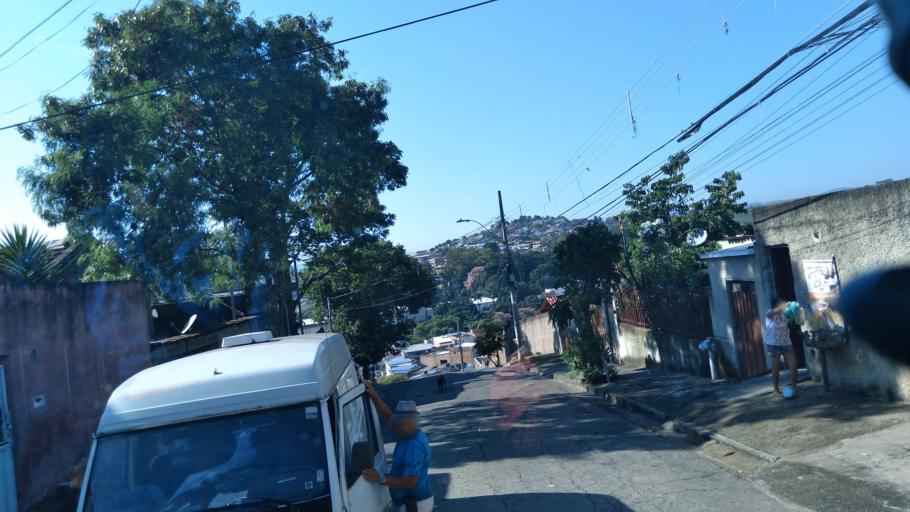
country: BR
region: Minas Gerais
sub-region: Contagem
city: Contagem
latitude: -19.8965
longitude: -44.0192
